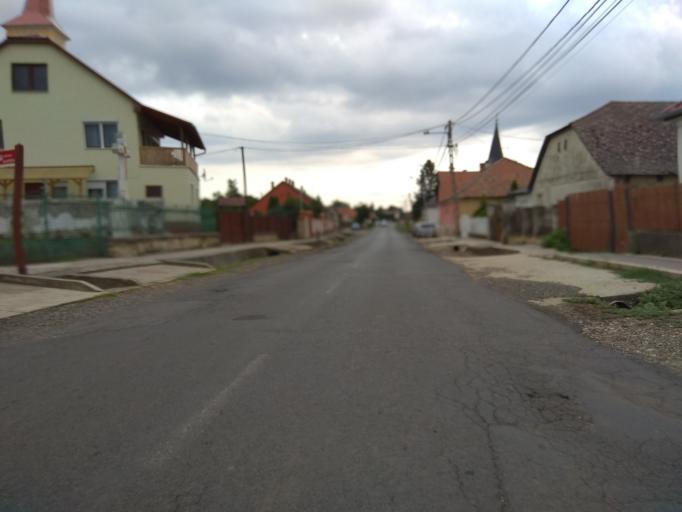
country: HU
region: Borsod-Abauj-Zemplen
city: Bekecs
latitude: 48.1591
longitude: 21.1527
